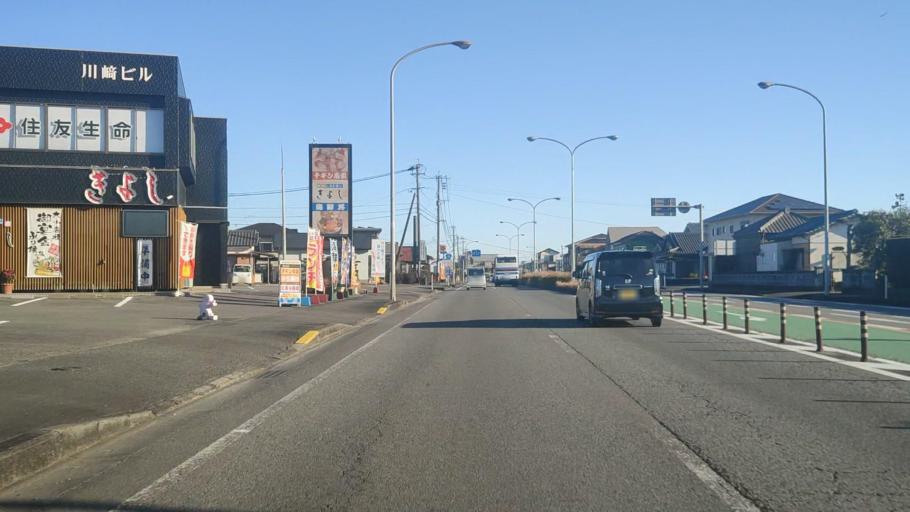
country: JP
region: Miyazaki
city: Nobeoka
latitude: 32.4581
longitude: 131.6457
